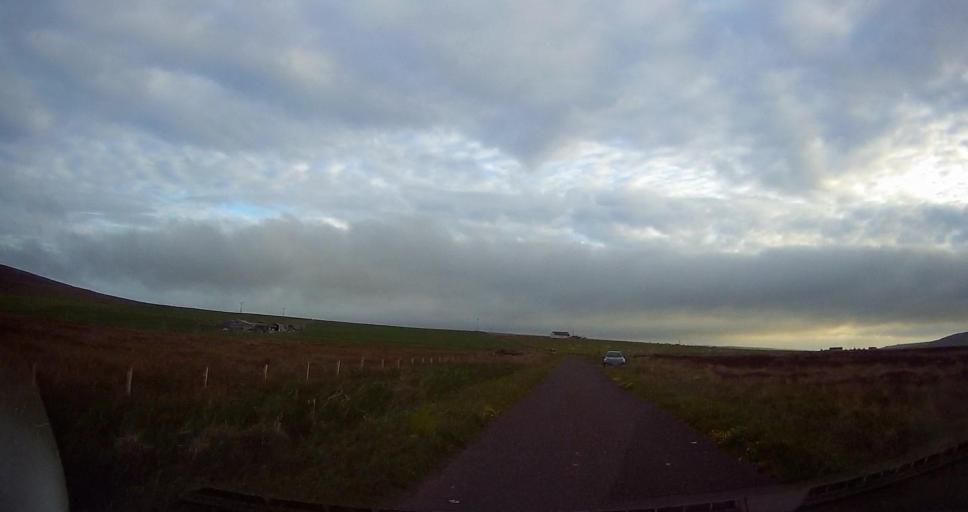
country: GB
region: Scotland
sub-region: Orkney Islands
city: Stromness
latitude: 59.1088
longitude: -3.2322
